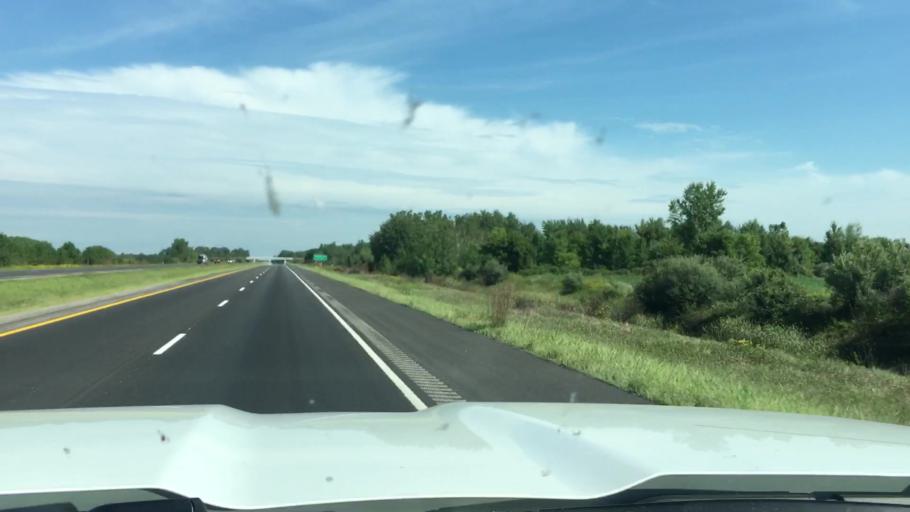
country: US
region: Michigan
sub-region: Saginaw County
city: Freeland
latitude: 43.5580
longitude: -84.1380
